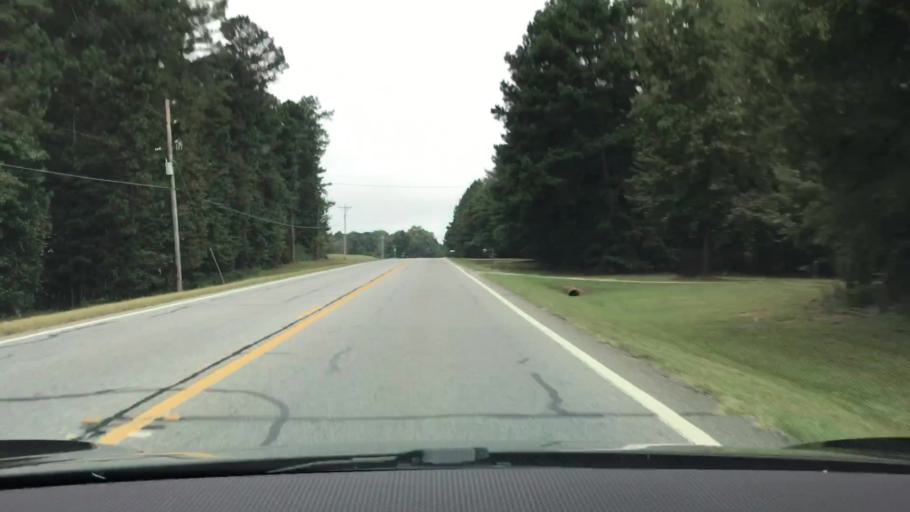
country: US
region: Georgia
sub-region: Oconee County
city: Watkinsville
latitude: 33.8078
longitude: -83.3493
